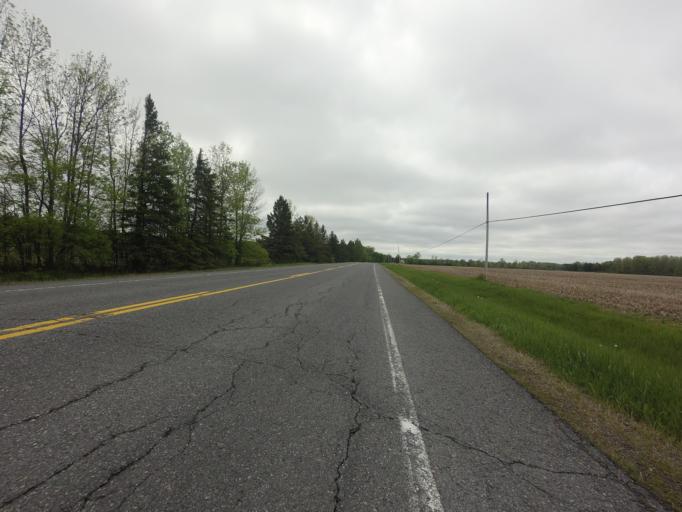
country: CA
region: Ontario
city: Casselman
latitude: 45.0556
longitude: -75.2018
